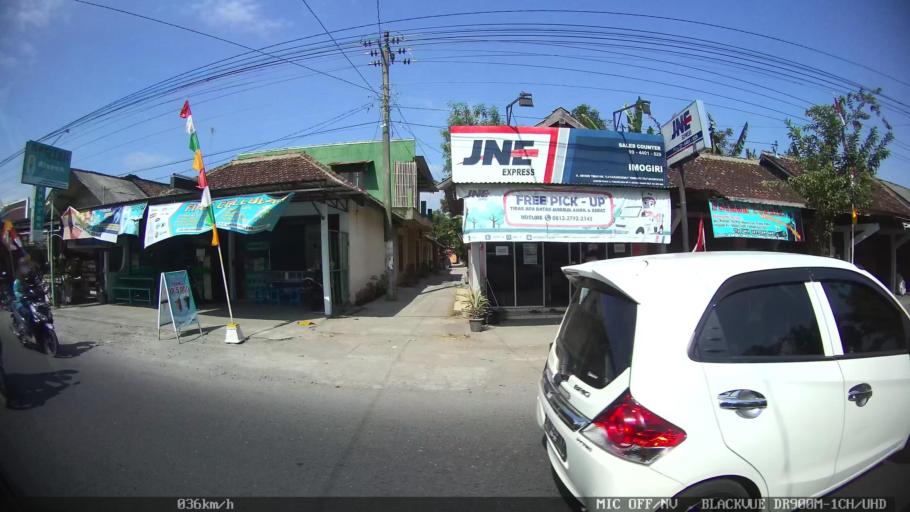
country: ID
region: Daerah Istimewa Yogyakarta
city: Sewon
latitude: -7.9005
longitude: 110.3841
